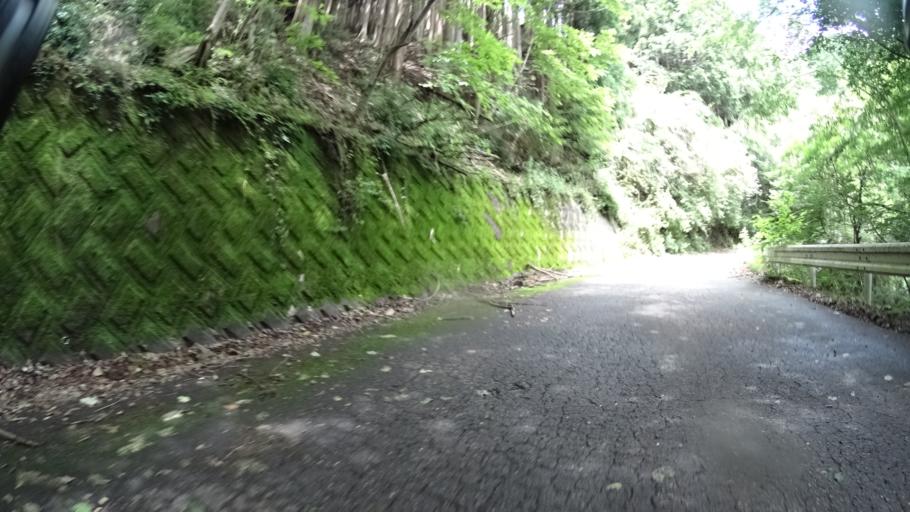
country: JP
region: Saitama
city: Chichibu
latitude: 35.8893
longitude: 139.1369
